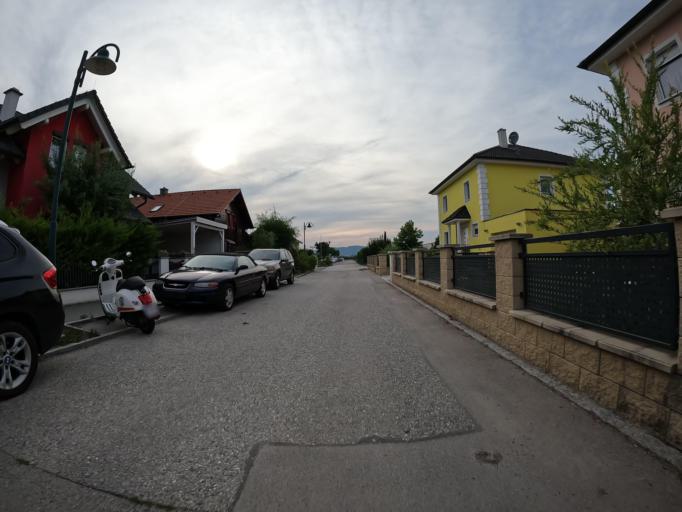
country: AT
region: Lower Austria
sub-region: Politischer Bezirk Baden
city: Trumau
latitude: 47.9984
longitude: 16.3378
